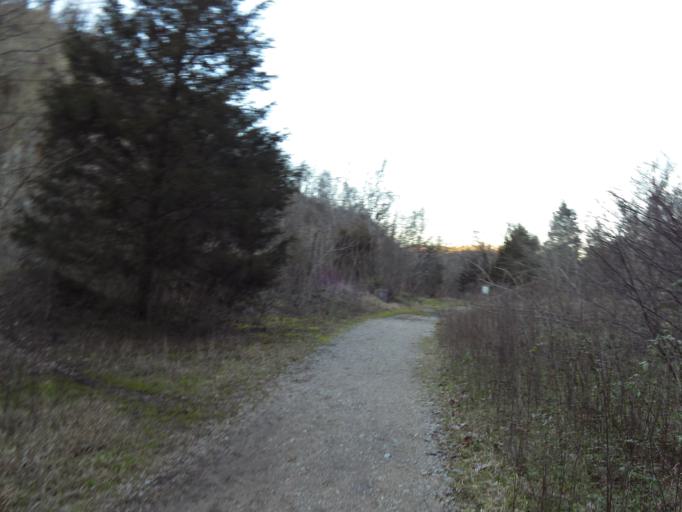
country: US
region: Tennessee
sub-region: Knox County
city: Knoxville
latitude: 35.9497
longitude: -83.8693
